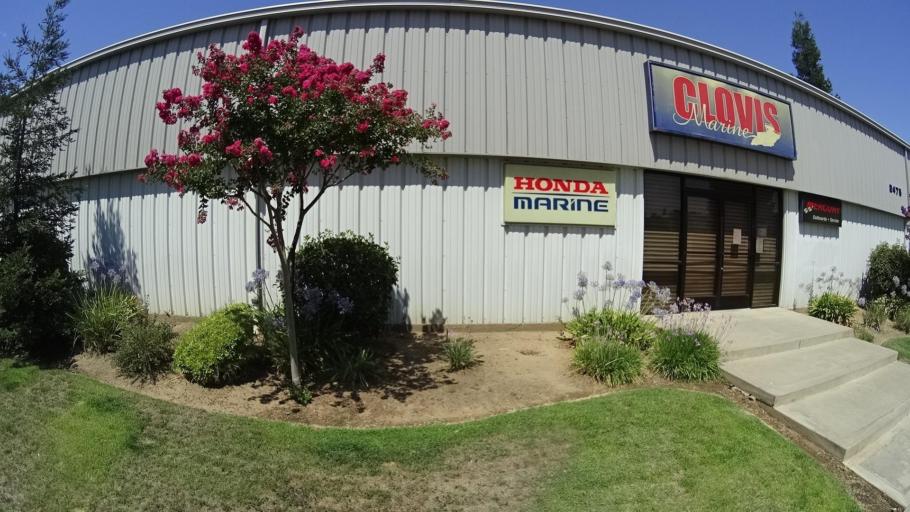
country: US
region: California
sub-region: Fresno County
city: Tarpey Village
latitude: 36.7729
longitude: -119.6876
